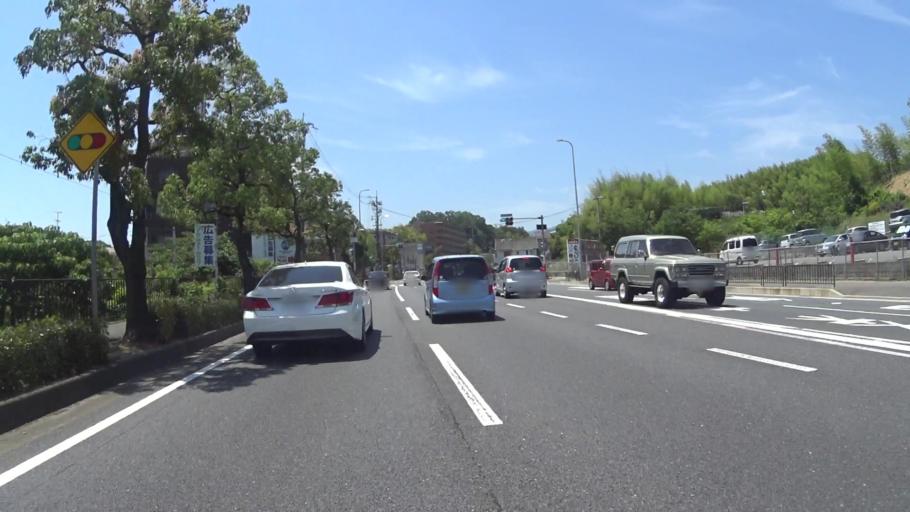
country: JP
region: Kyoto
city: Muko
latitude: 34.9751
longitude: 135.6878
